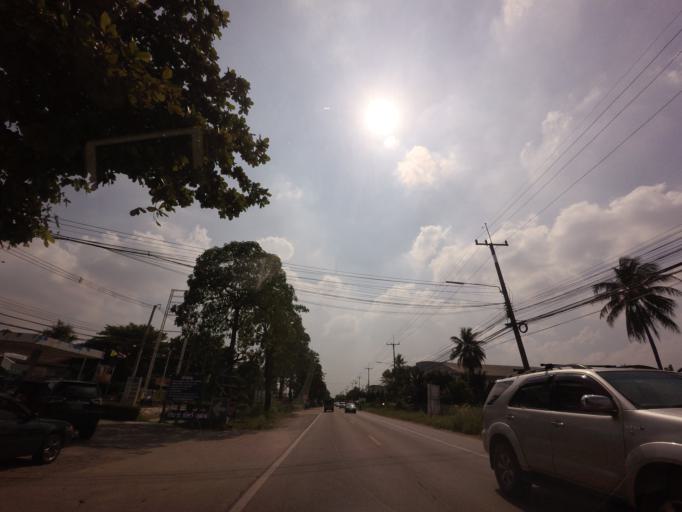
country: TH
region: Nakhon Pathom
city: Sam Phran
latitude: 13.7610
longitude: 100.2309
